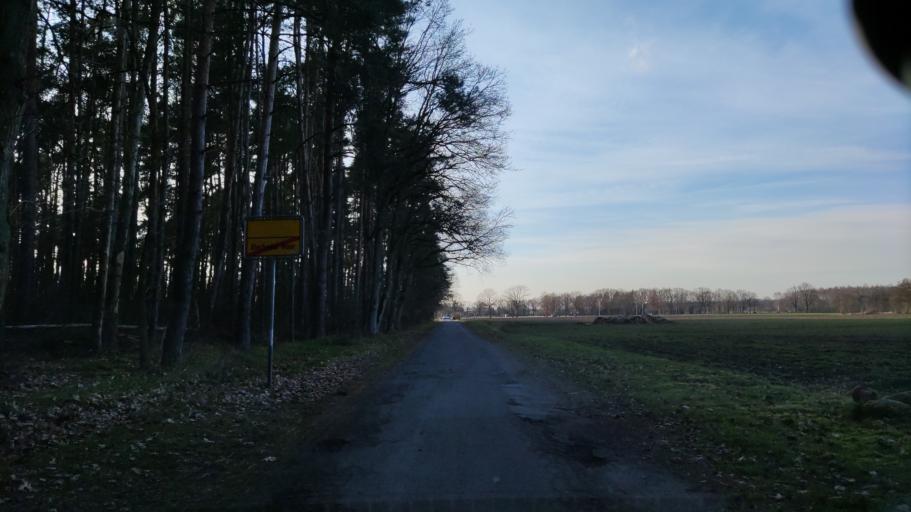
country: DE
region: Lower Saxony
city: Neetze
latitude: 53.2950
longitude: 10.6611
